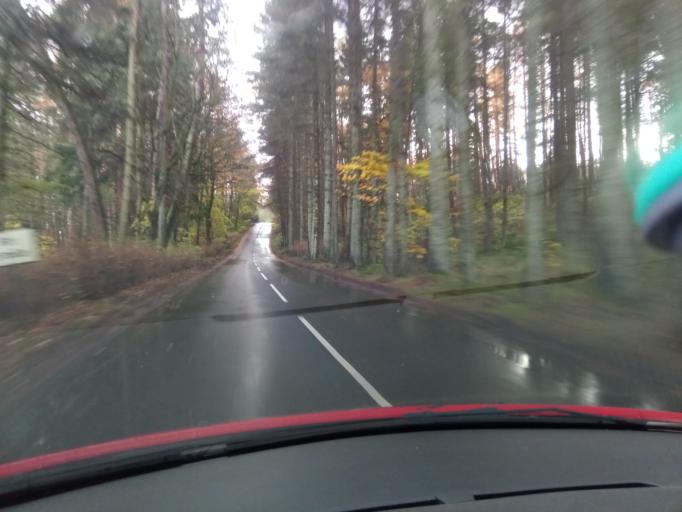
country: GB
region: England
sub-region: Northumberland
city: Birtley
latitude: 55.1013
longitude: -2.2280
